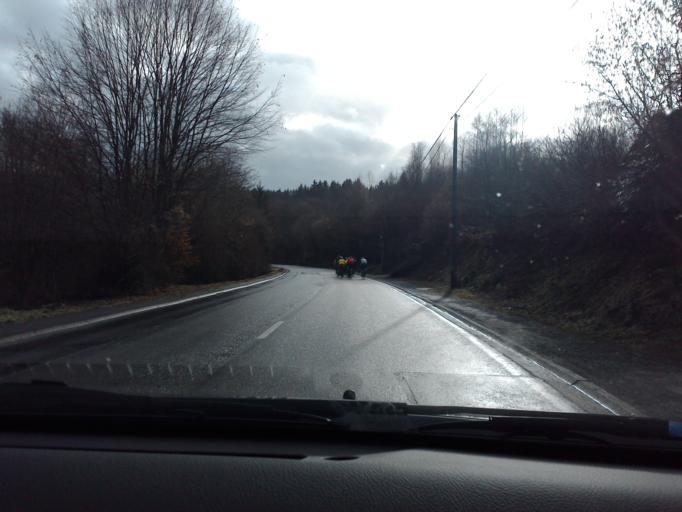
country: BE
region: Wallonia
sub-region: Province de Liege
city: Trois-Ponts
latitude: 50.3615
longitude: 5.8748
